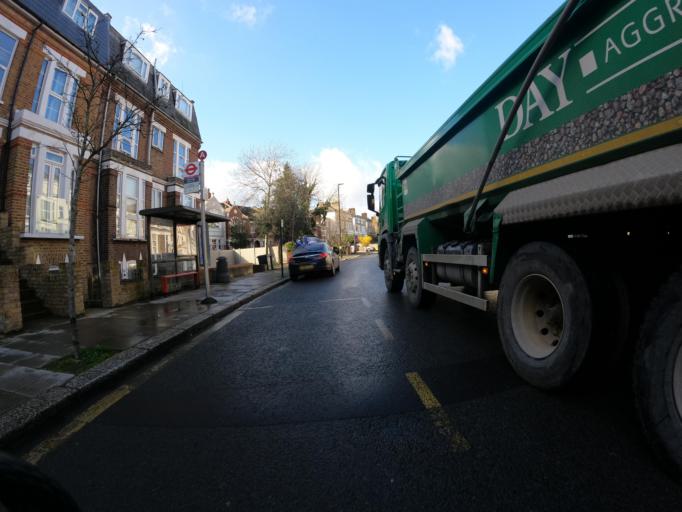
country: GB
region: England
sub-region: Greater London
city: Ealing
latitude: 51.5143
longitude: -0.3206
